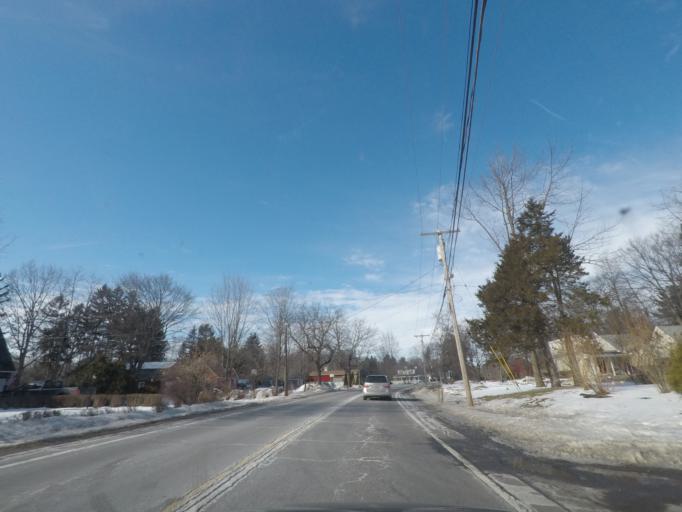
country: US
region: New York
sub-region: Albany County
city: Altamont
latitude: 42.7165
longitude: -73.9932
